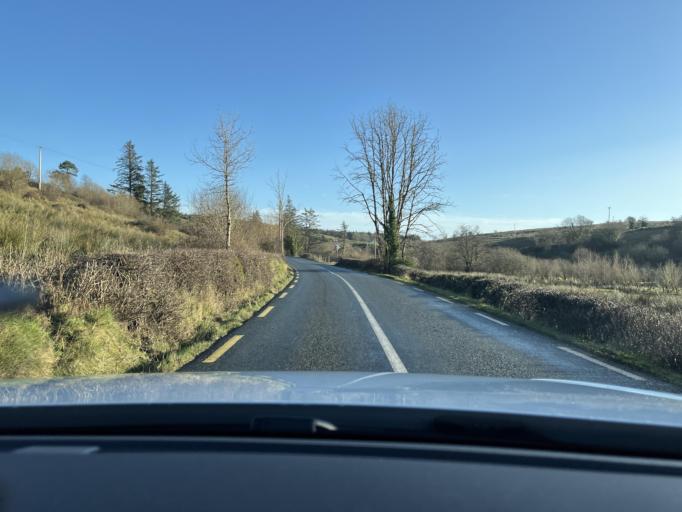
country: IE
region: Connaught
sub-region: County Leitrim
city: Manorhamilton
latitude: 54.2364
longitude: -8.2131
